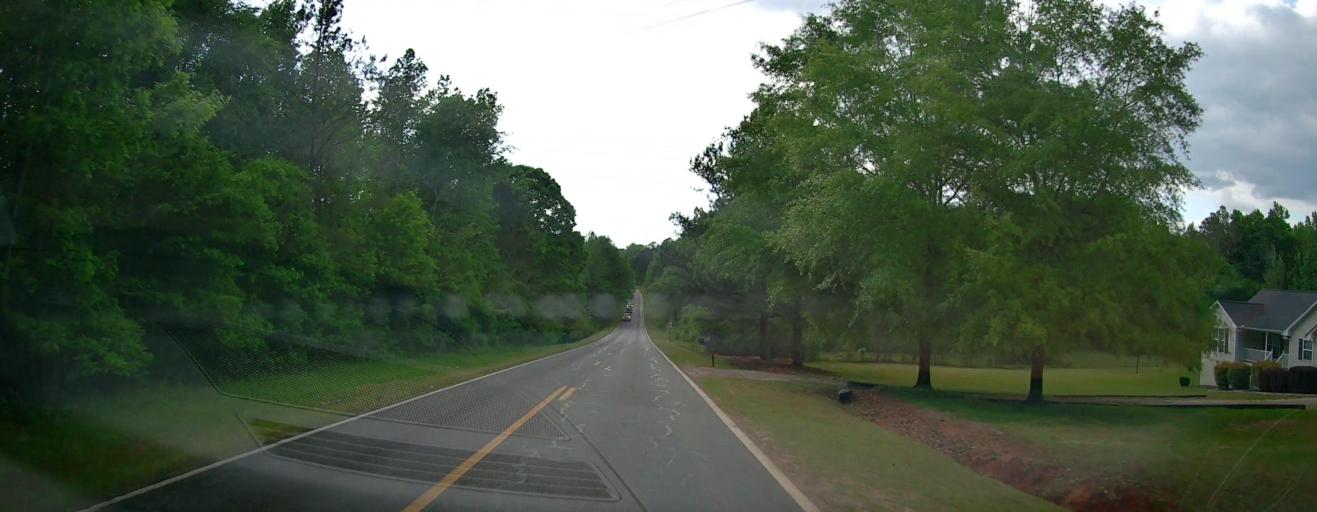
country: US
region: Georgia
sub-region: Baldwin County
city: Hardwick
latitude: 33.0625
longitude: -83.1440
